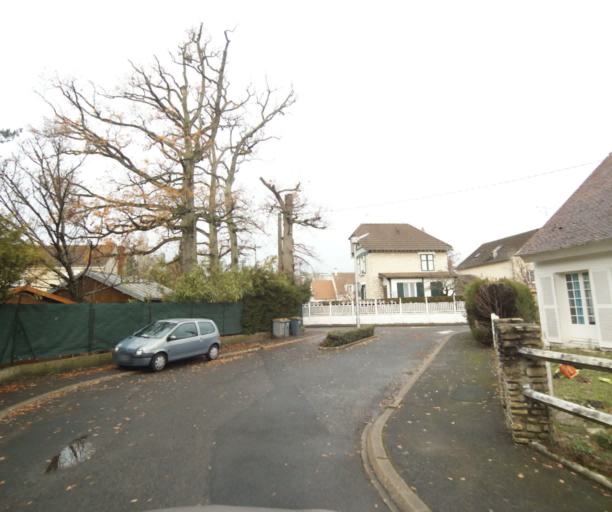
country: FR
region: Ile-de-France
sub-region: Departement de Seine-et-Marne
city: Avon
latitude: 48.4018
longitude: 2.7240
